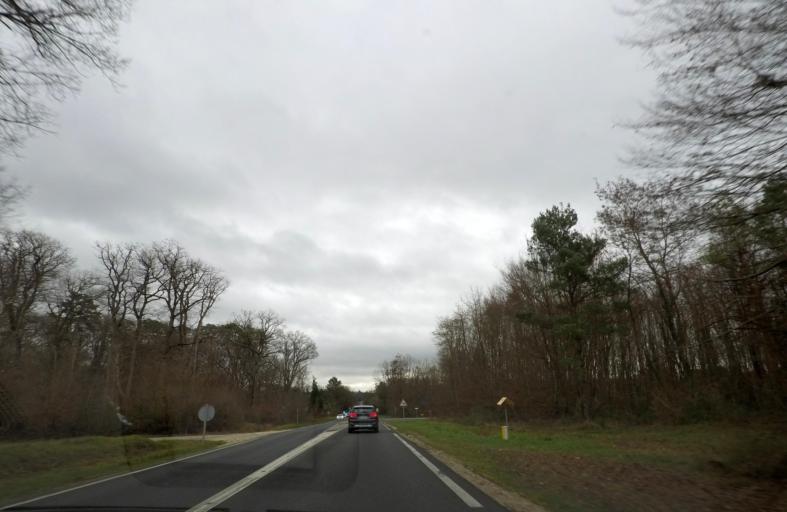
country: FR
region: Centre
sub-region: Departement du Loir-et-Cher
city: Cellettes
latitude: 47.5353
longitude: 1.4143
